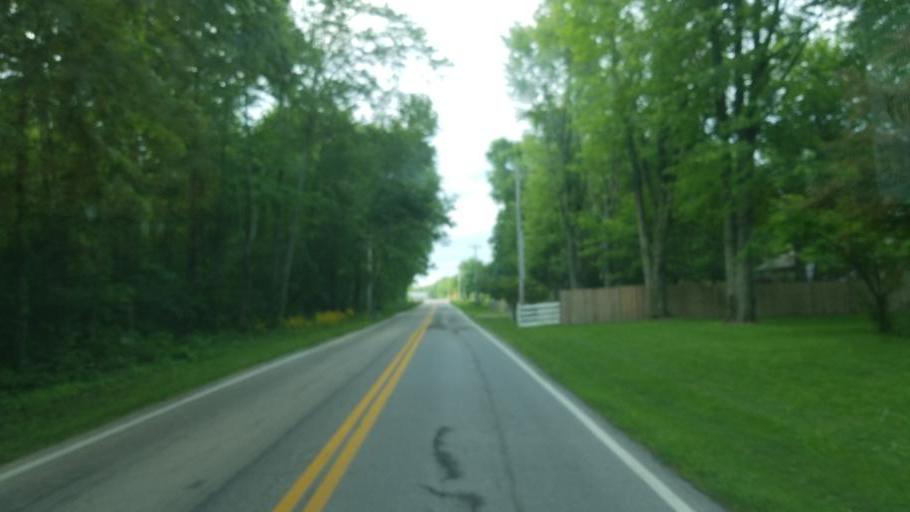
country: US
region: Ohio
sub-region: Knox County
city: Centerburg
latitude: 40.3154
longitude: -82.7835
